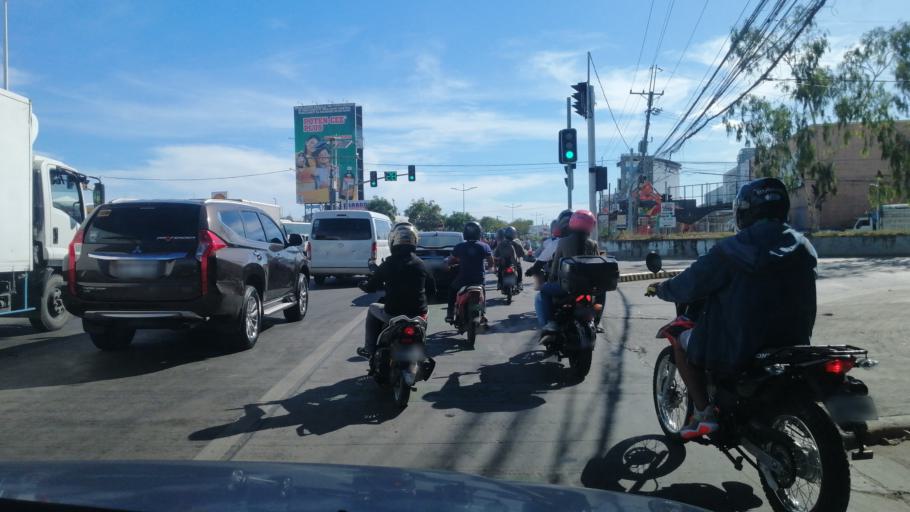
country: PH
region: Central Visayas
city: Mandaue City
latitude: 10.3170
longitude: 123.9289
